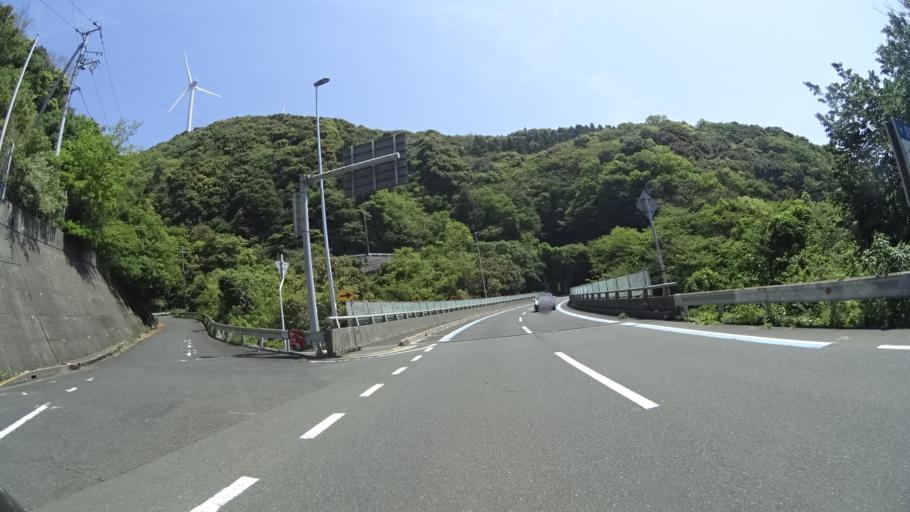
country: JP
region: Ehime
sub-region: Nishiuwa-gun
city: Ikata-cho
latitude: 33.4322
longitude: 132.2133
